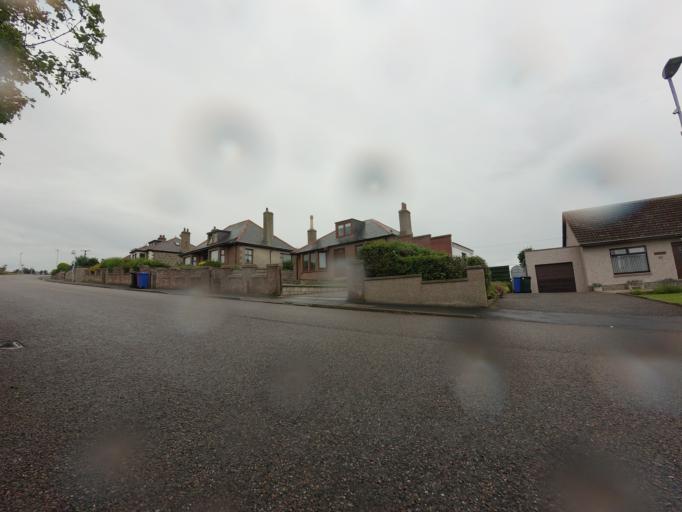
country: GB
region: Scotland
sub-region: Moray
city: Findochty
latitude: 57.6969
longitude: -2.8996
